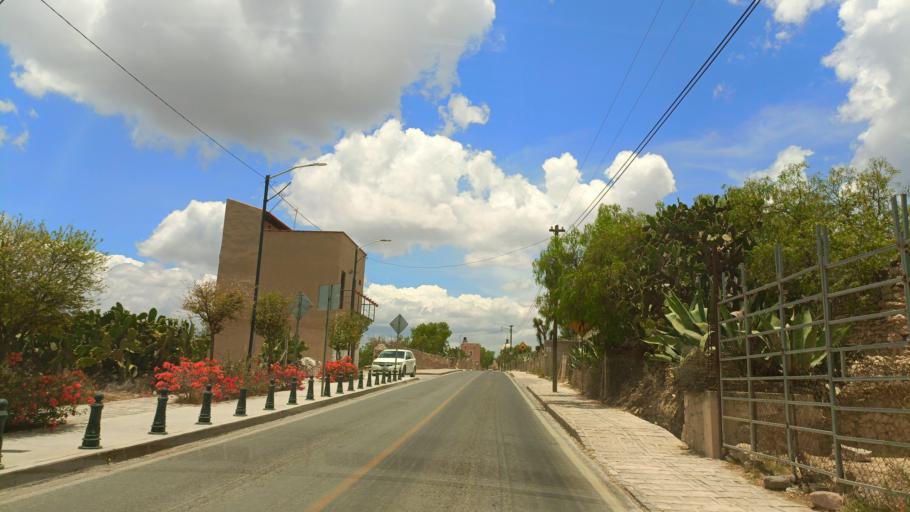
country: MX
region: Guanajuato
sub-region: San Luis de la Paz
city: San Ignacio
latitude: 21.2275
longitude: -100.4921
